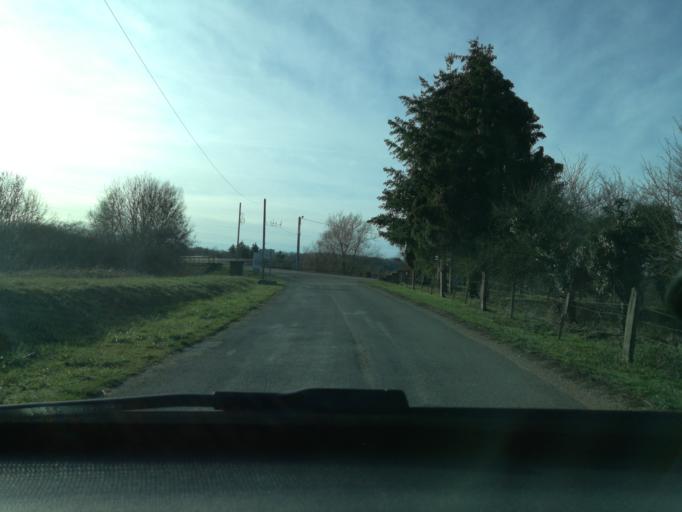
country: FR
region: Lorraine
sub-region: Departement de la Meuse
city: Revigny-sur-Ornain
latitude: 48.8211
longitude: 5.0437
